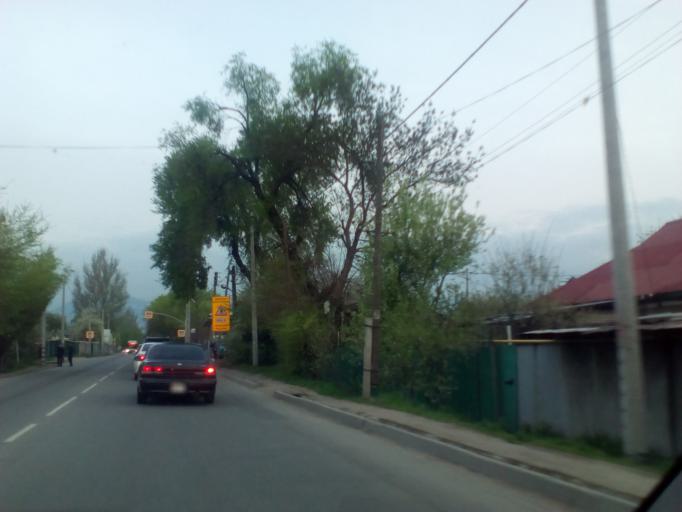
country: KZ
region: Almaty Qalasy
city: Almaty
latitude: 43.2297
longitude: 76.8269
